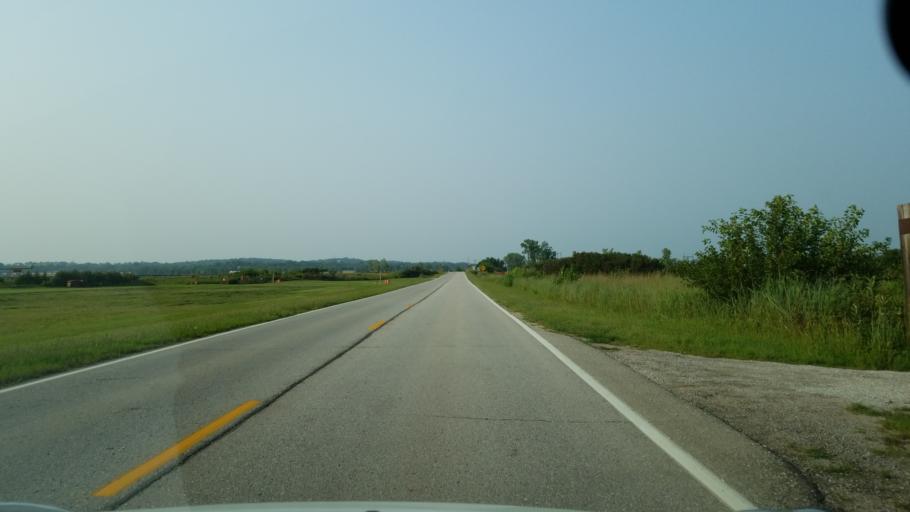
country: US
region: Nebraska
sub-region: Sarpy County
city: Bellevue
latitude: 41.1069
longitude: -95.8899
